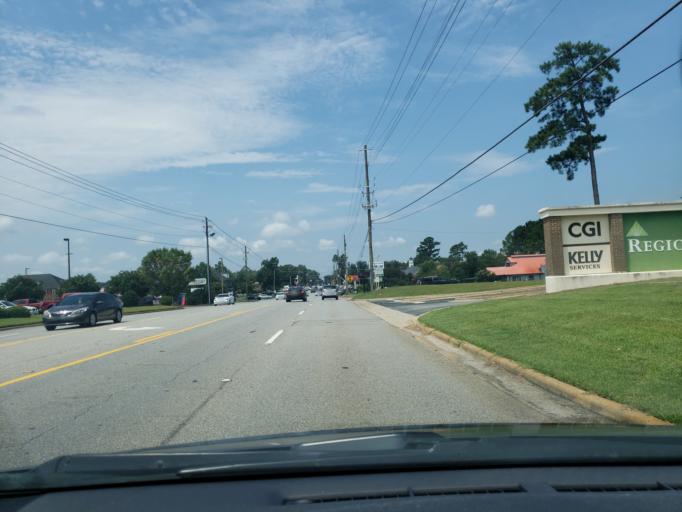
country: US
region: Georgia
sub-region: Dougherty County
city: Albany
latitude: 31.6136
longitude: -84.2200
